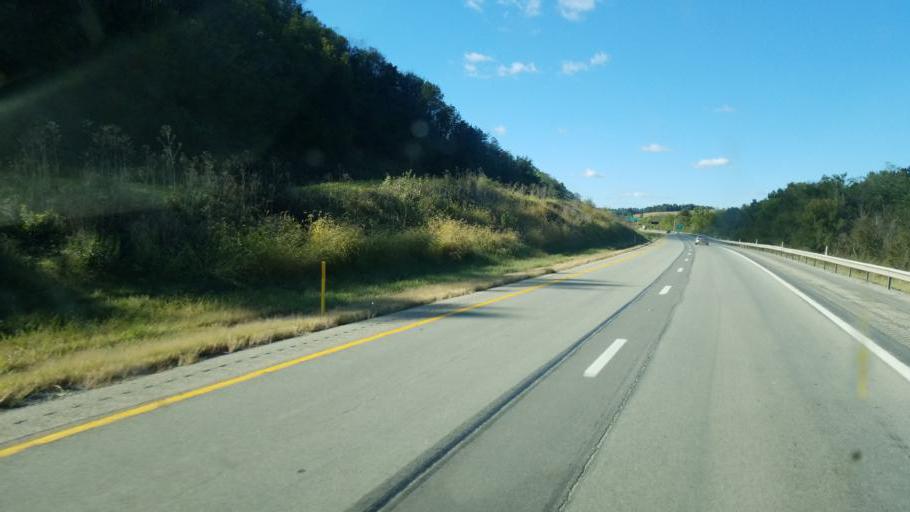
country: US
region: Pennsylvania
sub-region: Washington County
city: East Washington
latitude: 40.1182
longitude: -80.2037
